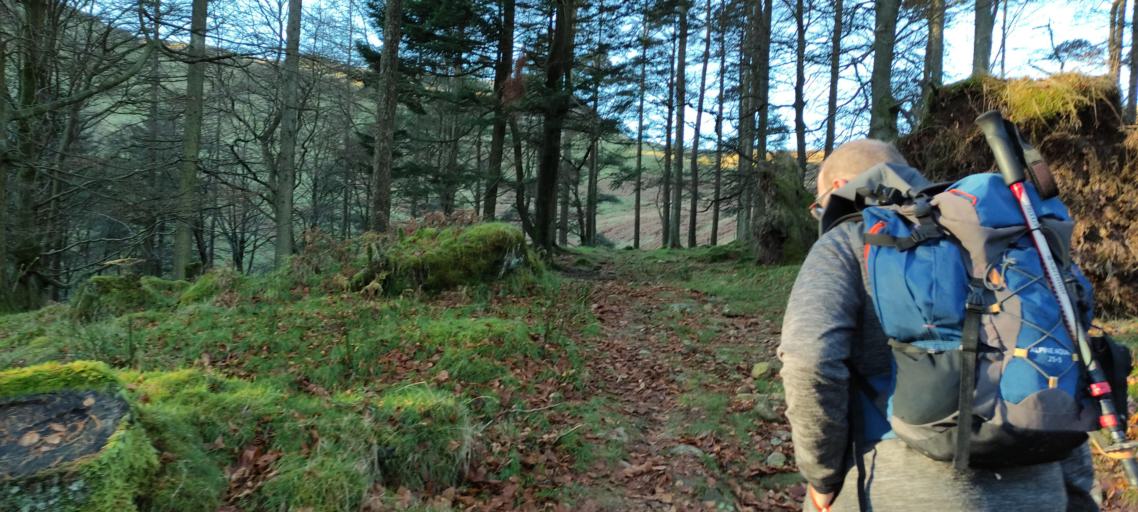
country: GB
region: England
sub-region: Cumbria
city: Keswick
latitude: 54.5150
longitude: -3.0779
